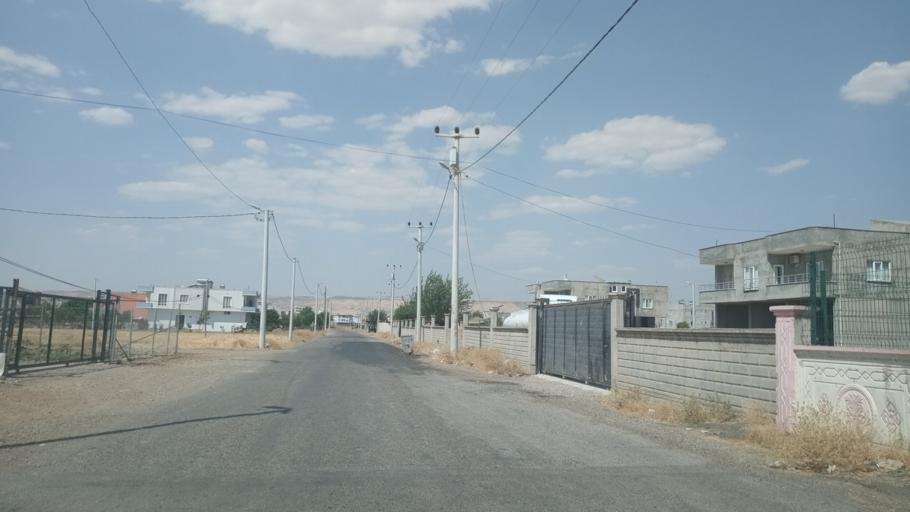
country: TR
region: Batman
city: Binatli
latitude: 37.8400
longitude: 41.2100
